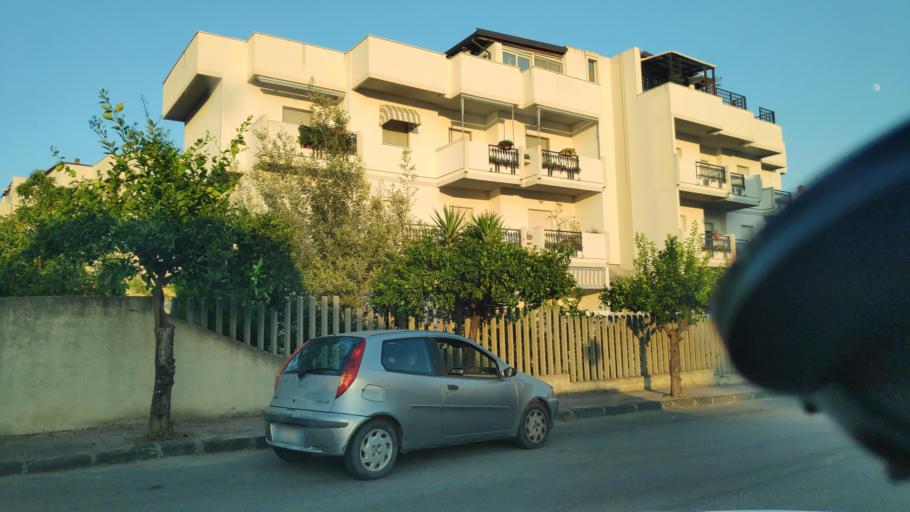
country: IT
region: Calabria
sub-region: Provincia di Reggio Calabria
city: Roccella Ionica
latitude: 38.3212
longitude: 16.3948
